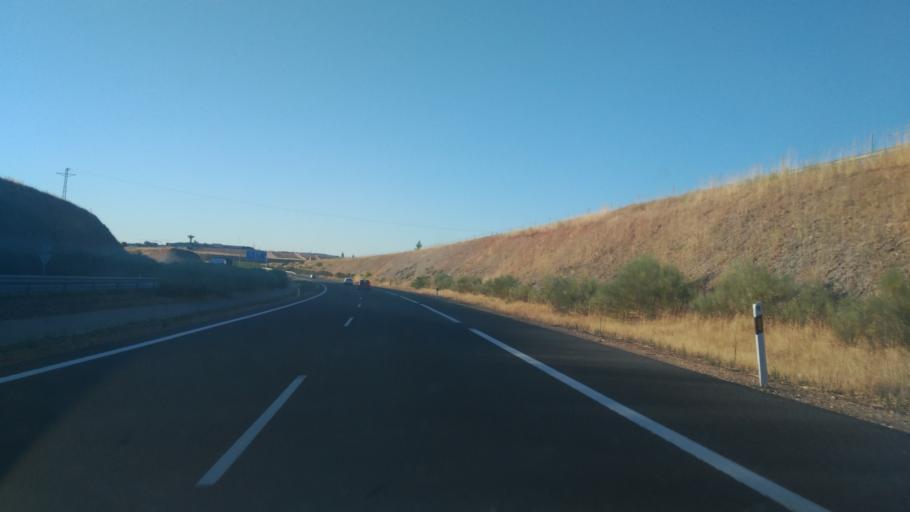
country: ES
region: Castille and Leon
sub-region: Provincia de Salamanca
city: Arapiles
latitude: 40.9112
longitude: -5.6605
